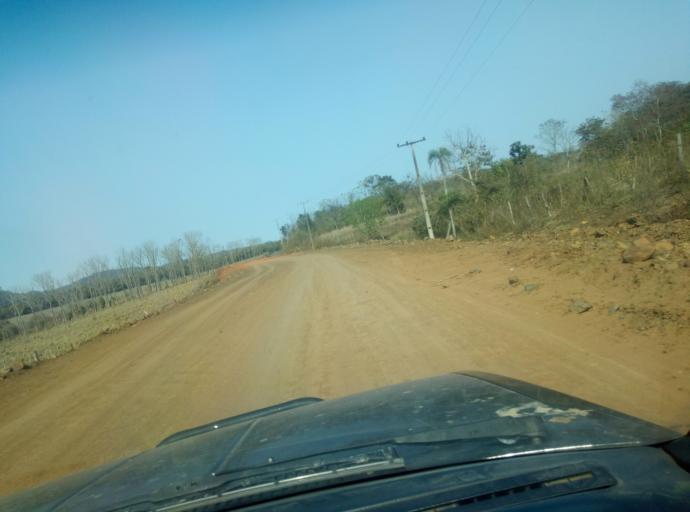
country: PY
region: Caaguazu
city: Coronel Oviedo
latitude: -25.3338
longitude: -56.3145
